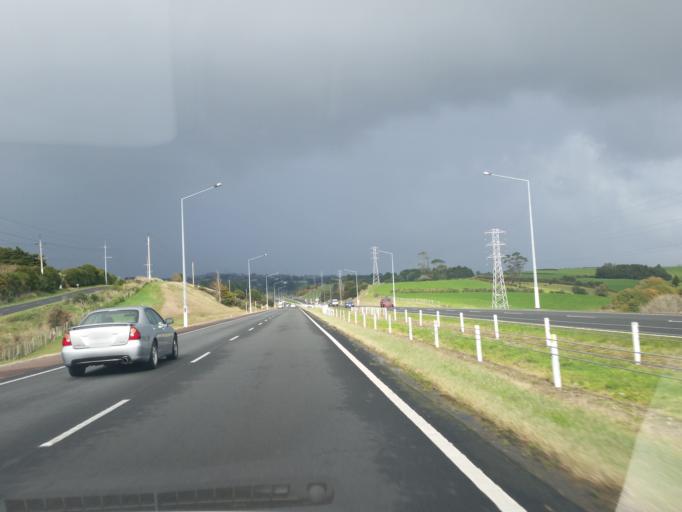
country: NZ
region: Auckland
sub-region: Auckland
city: Pukekohe East
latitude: -37.1527
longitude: 174.9754
